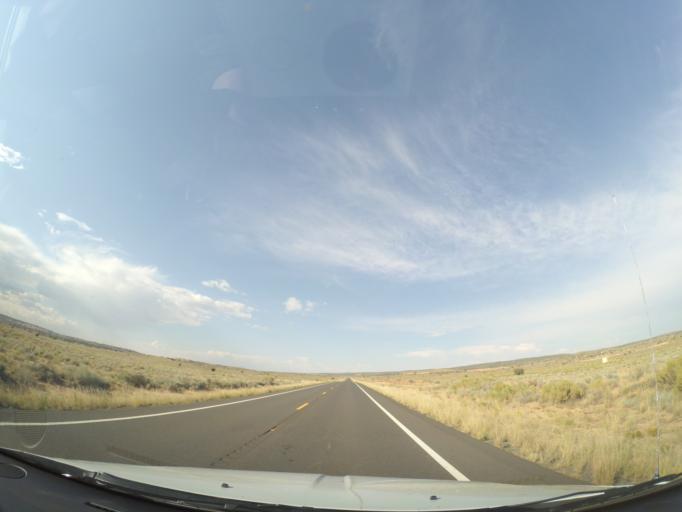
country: US
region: Arizona
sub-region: Coconino County
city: Kaibito
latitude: 36.4719
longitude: -111.4183
